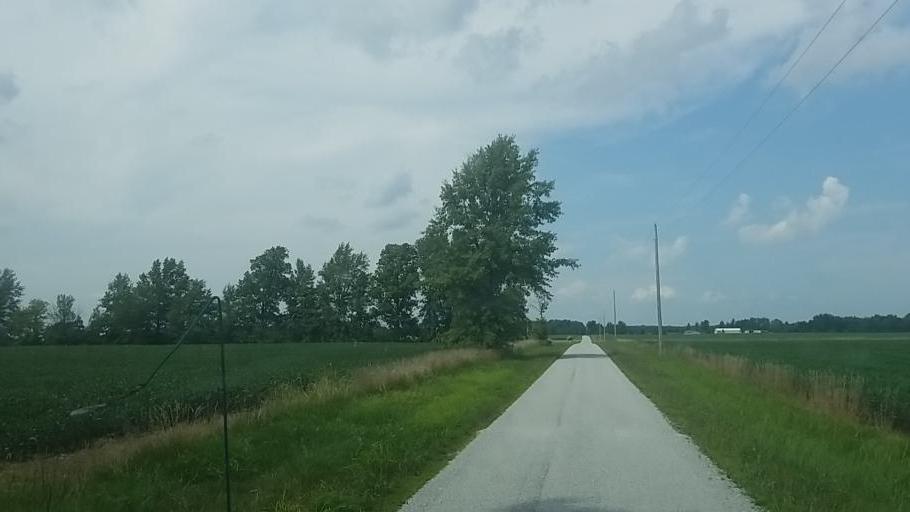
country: US
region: Ohio
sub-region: Hardin County
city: Forest
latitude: 40.7665
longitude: -83.5954
